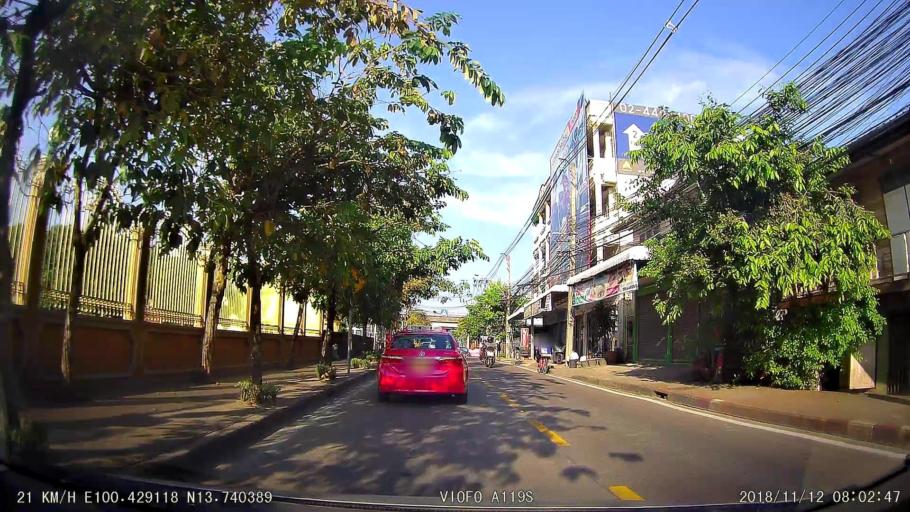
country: TH
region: Bangkok
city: Phasi Charoen
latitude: 13.7404
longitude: 100.4290
